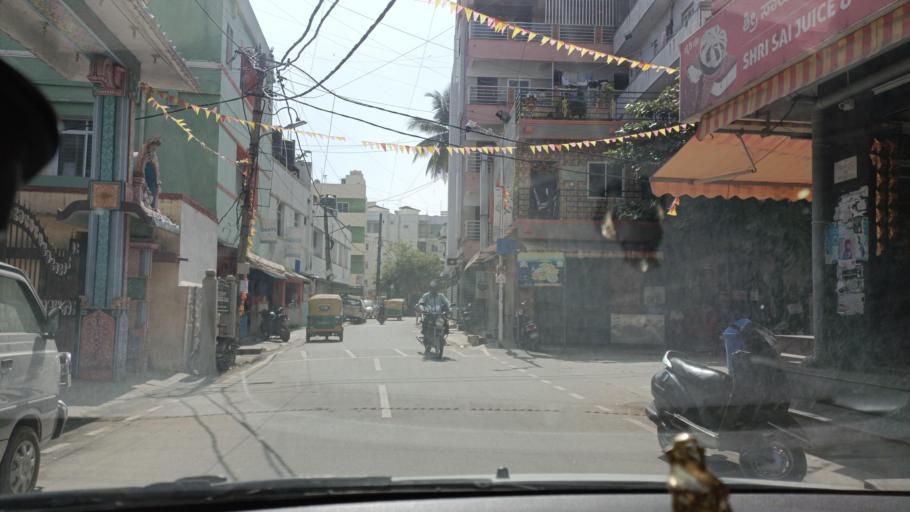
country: IN
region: Karnataka
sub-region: Bangalore Urban
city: Bangalore
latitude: 12.9181
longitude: 77.6182
